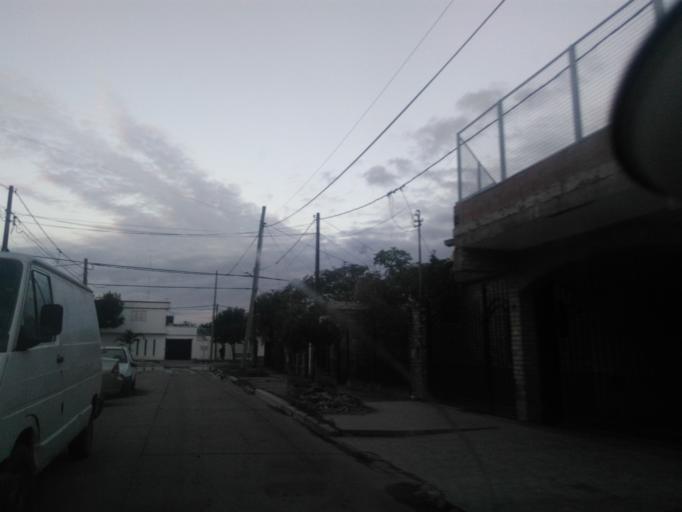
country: AR
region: Chaco
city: Resistencia
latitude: -27.4552
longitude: -59.0162
